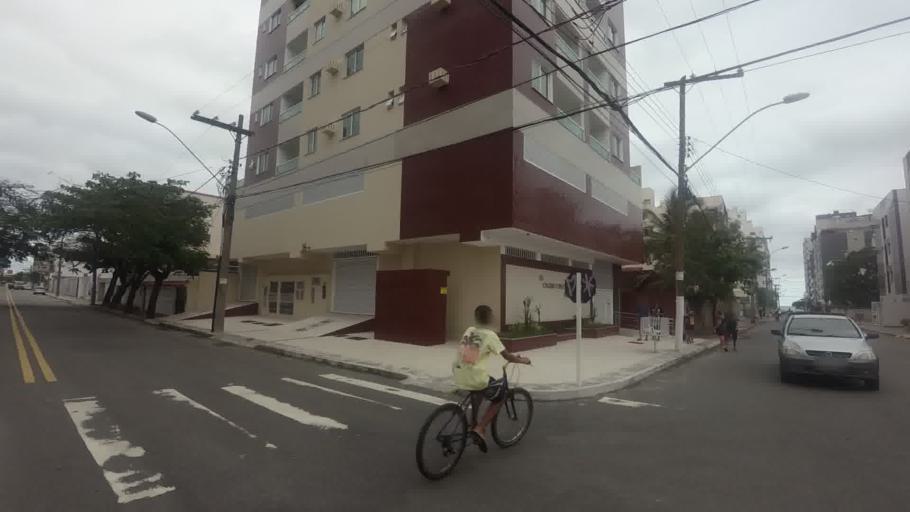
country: BR
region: Espirito Santo
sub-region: Guarapari
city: Guarapari
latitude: -20.6517
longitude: -40.4888
